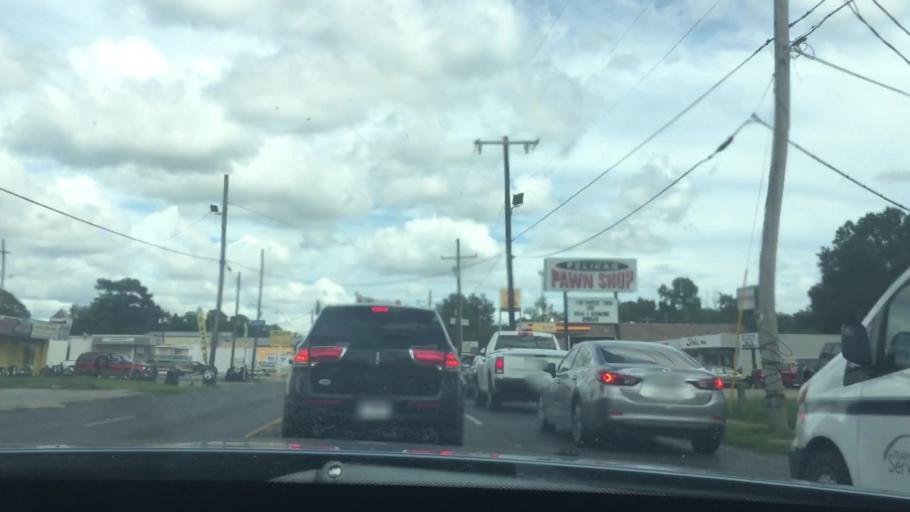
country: US
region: Louisiana
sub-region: East Baton Rouge Parish
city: Baton Rouge
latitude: 30.4499
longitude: -91.1682
